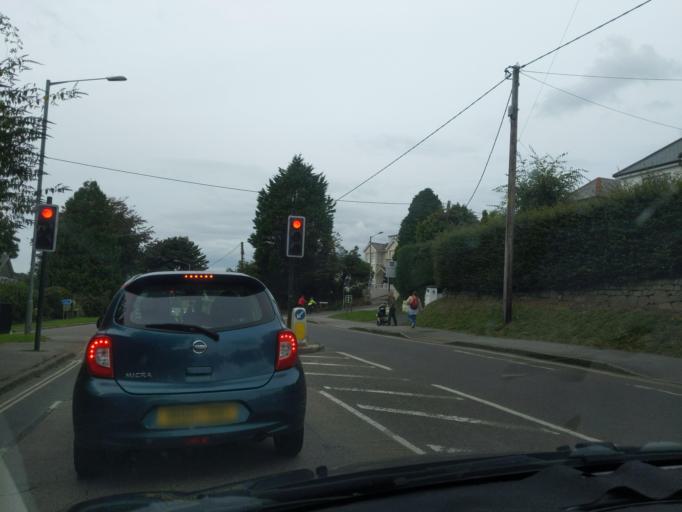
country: GB
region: England
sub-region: Cornwall
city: St Austell
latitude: 50.3340
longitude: -4.7858
